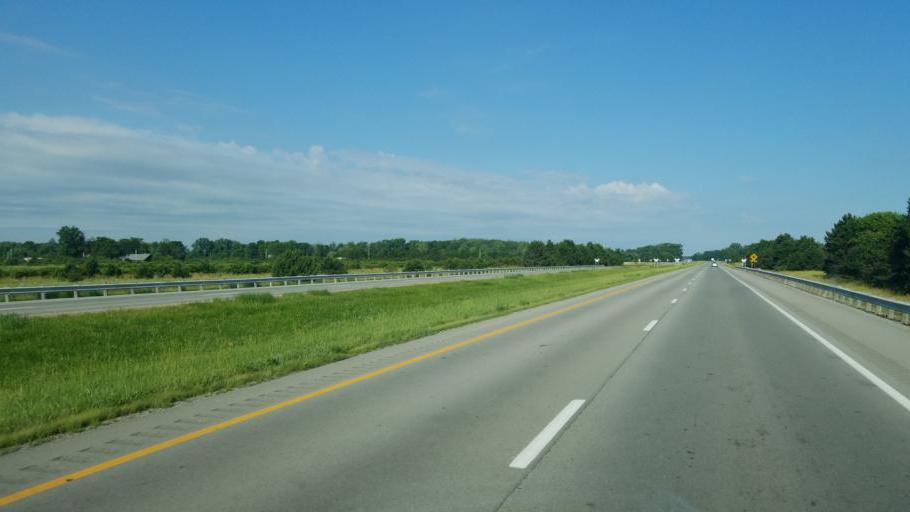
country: US
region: Ohio
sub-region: Hancock County
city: Findlay
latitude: 40.9820
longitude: -83.5306
